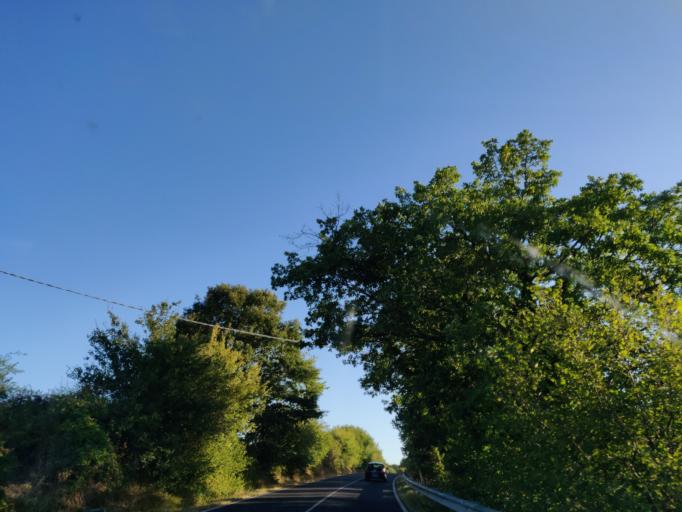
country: IT
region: Latium
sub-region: Provincia di Viterbo
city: Gradoli
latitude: 42.6454
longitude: 11.8400
